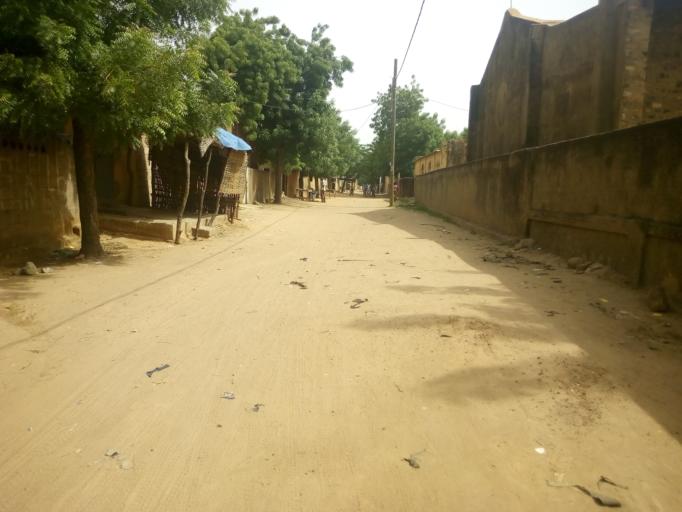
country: ML
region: Kayes
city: Kayes
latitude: 14.4391
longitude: -11.4381
